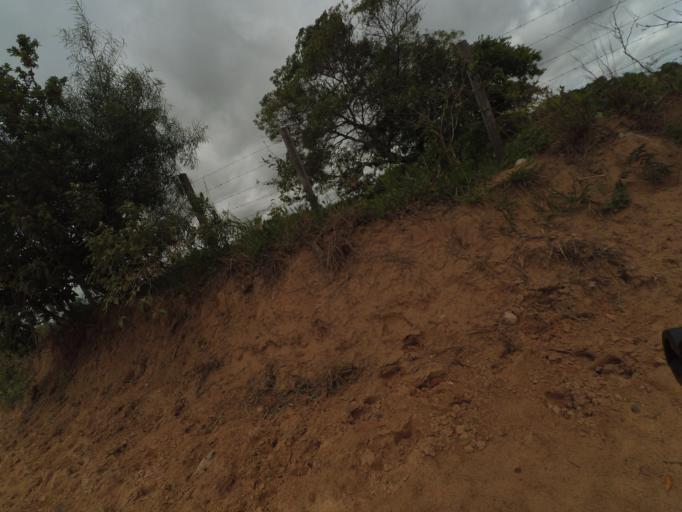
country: BO
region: Santa Cruz
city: Santa Rita
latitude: -17.9056
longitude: -63.2441
